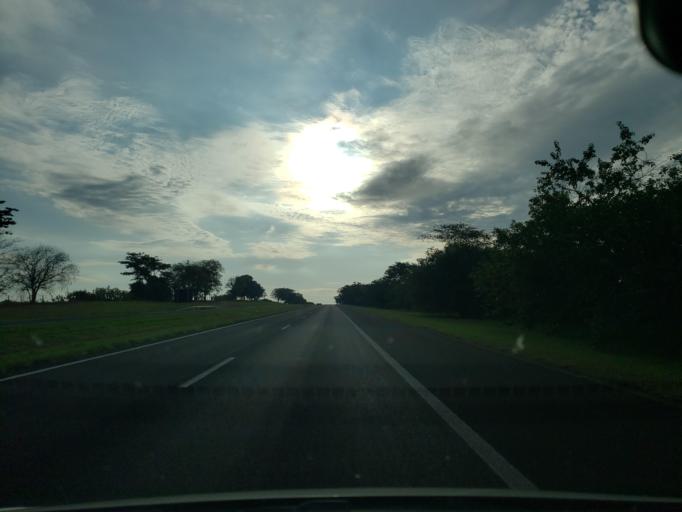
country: BR
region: Sao Paulo
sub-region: Mirandopolis
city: Mirandopolis
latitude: -21.1159
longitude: -51.0157
